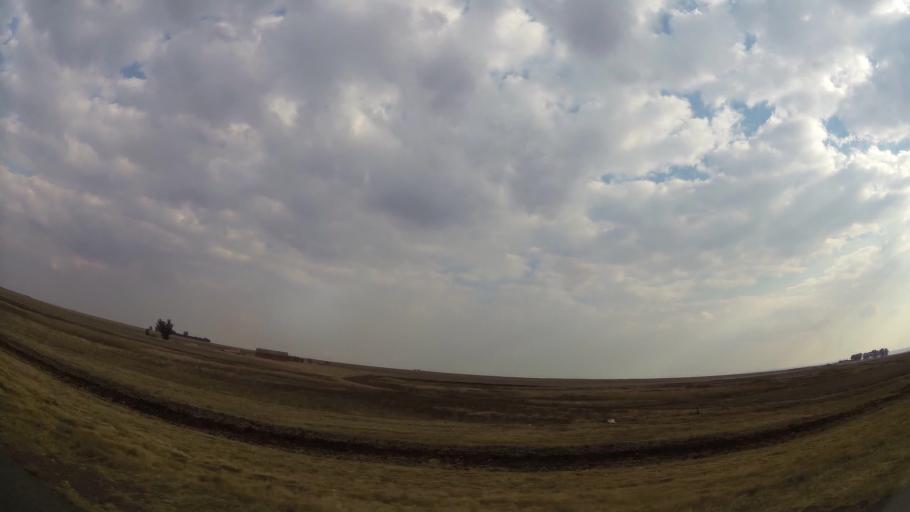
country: ZA
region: Gauteng
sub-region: Ekurhuleni Metropolitan Municipality
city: Nigel
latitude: -26.3154
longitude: 28.5835
